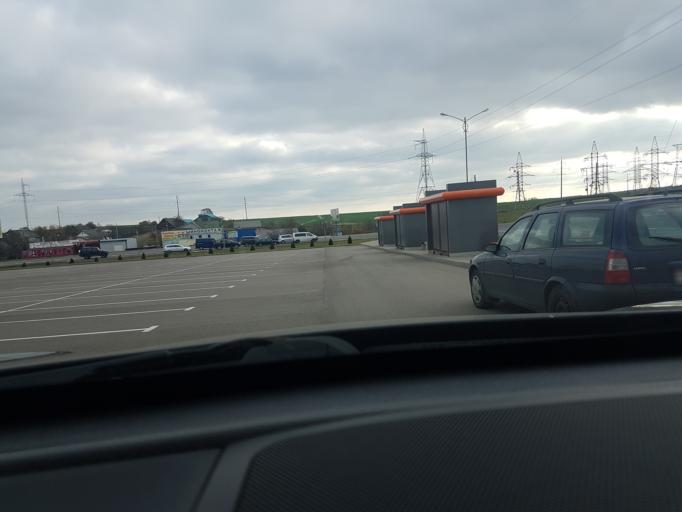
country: BY
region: Minsk
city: Malinovka
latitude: 53.8480
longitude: 27.4334
